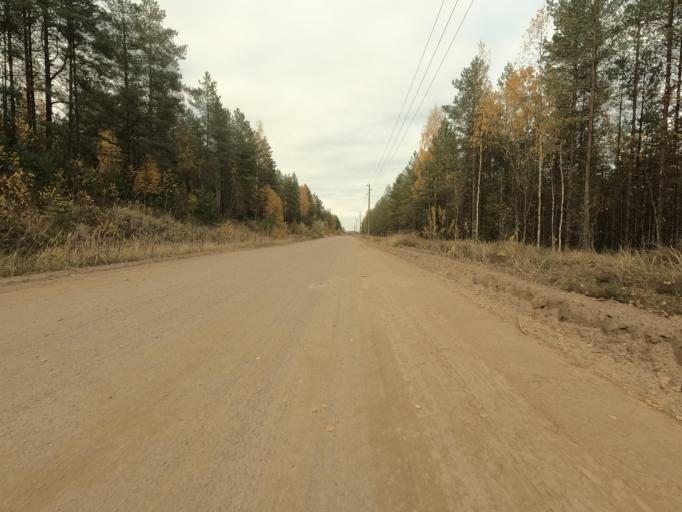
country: RU
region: Leningrad
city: Priladozhskiy
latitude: 59.6958
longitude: 31.3616
